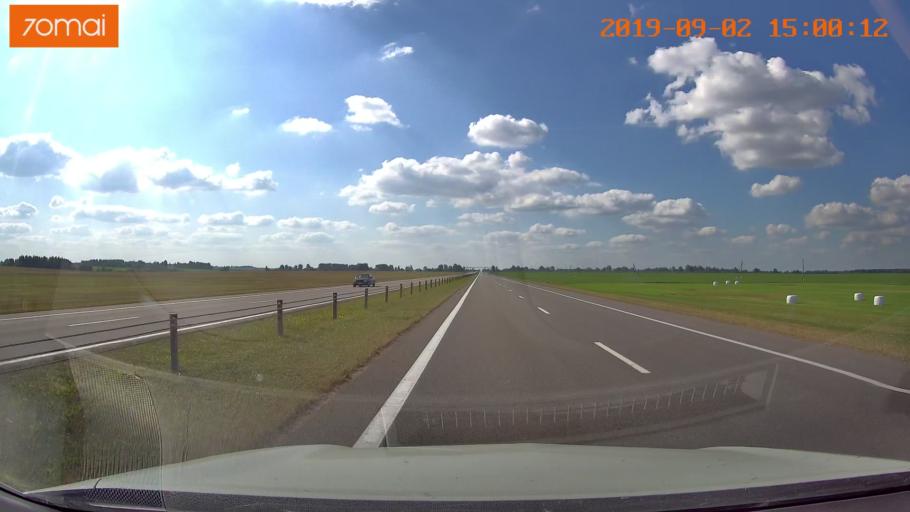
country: BY
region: Mogilev
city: Vishow
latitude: 53.9774
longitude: 30.0848
